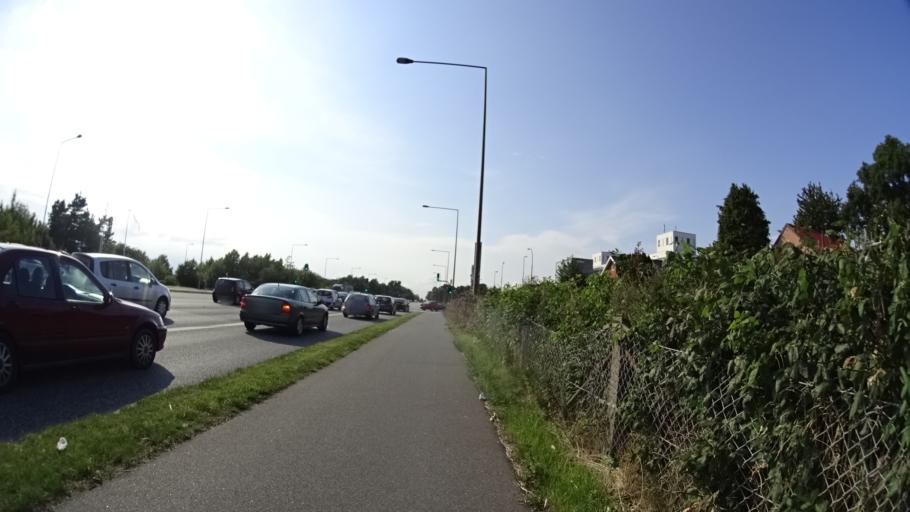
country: DK
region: Central Jutland
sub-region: Arhus Kommune
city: Stavtrup
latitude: 56.1532
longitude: 10.1378
